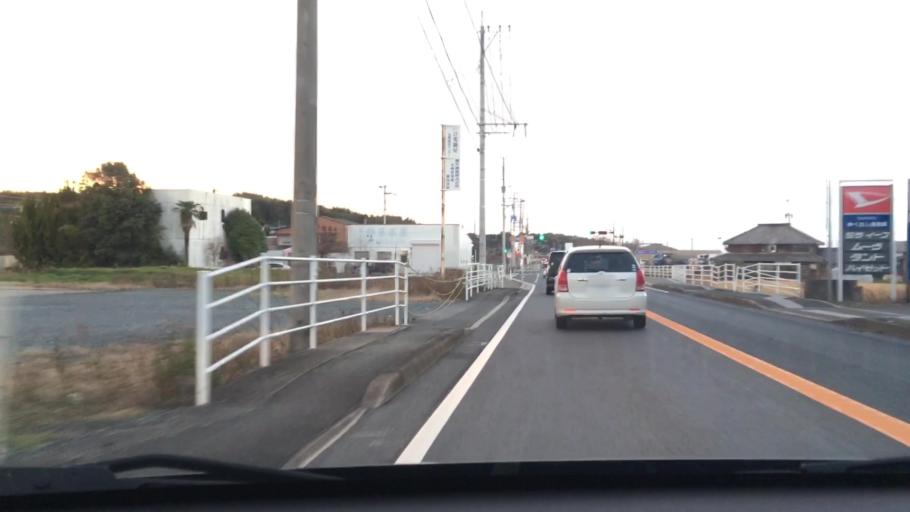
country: JP
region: Fukuoka
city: Shiida
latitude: 33.6327
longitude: 131.0801
